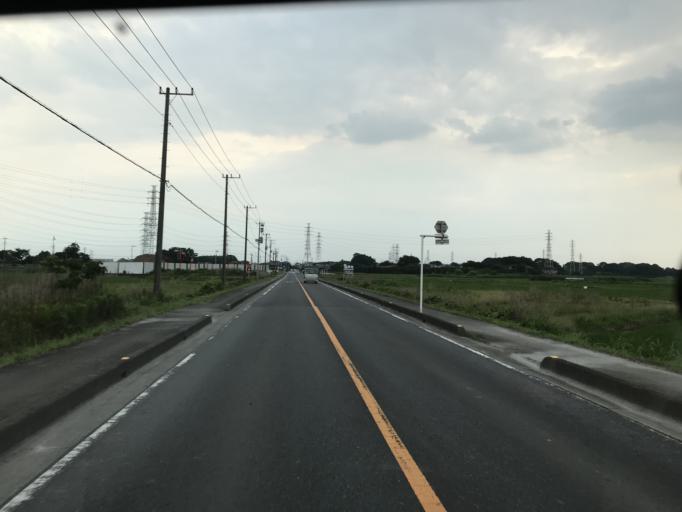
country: JP
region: Saitama
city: Shiraoka
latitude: 36.0130
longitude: 139.6856
